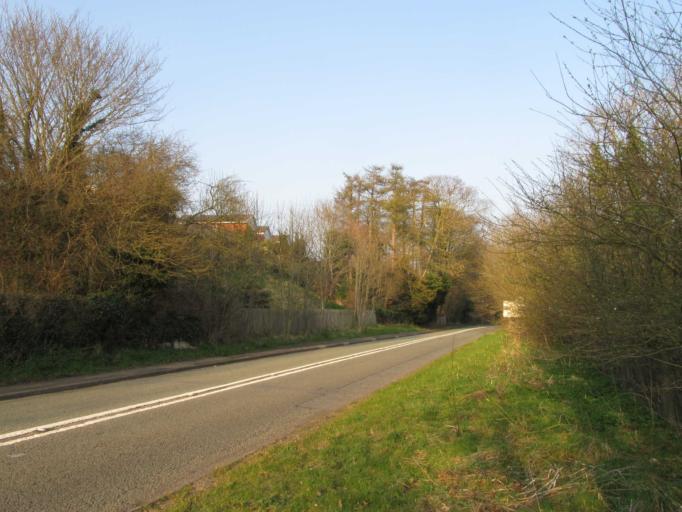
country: GB
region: Wales
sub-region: County of Flintshire
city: Buckley
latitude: 53.1994
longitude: -3.0894
